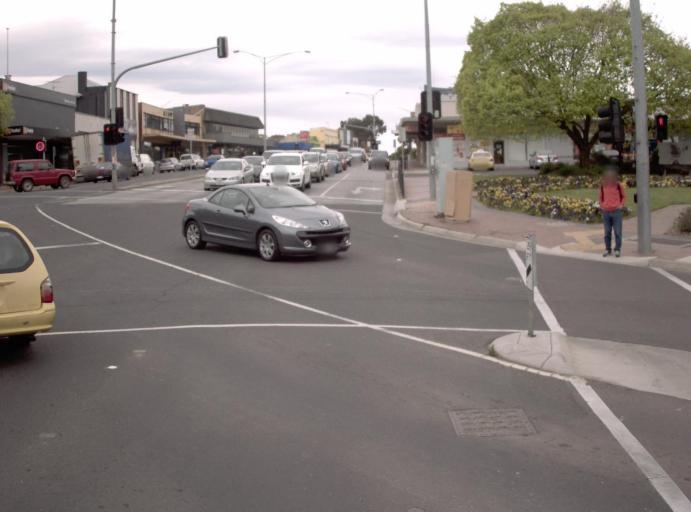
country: AU
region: Victoria
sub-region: Maroondah
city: Ringwood East
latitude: -37.8160
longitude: 145.2272
